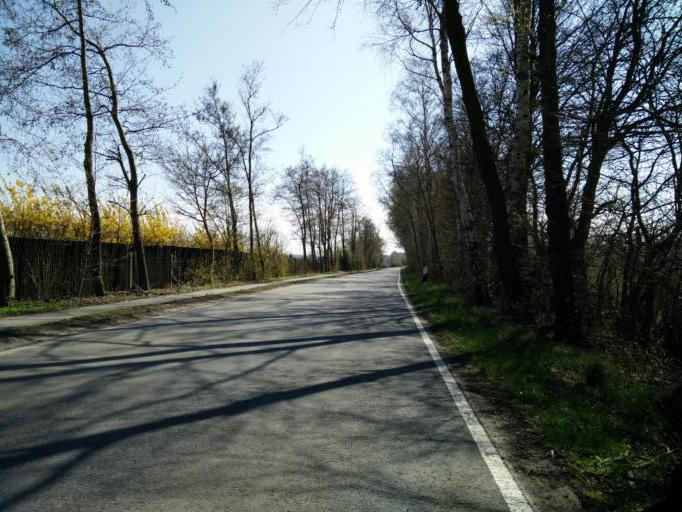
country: DE
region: Mecklenburg-Vorpommern
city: Elmenhorst
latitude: 54.1329
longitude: 12.0333
